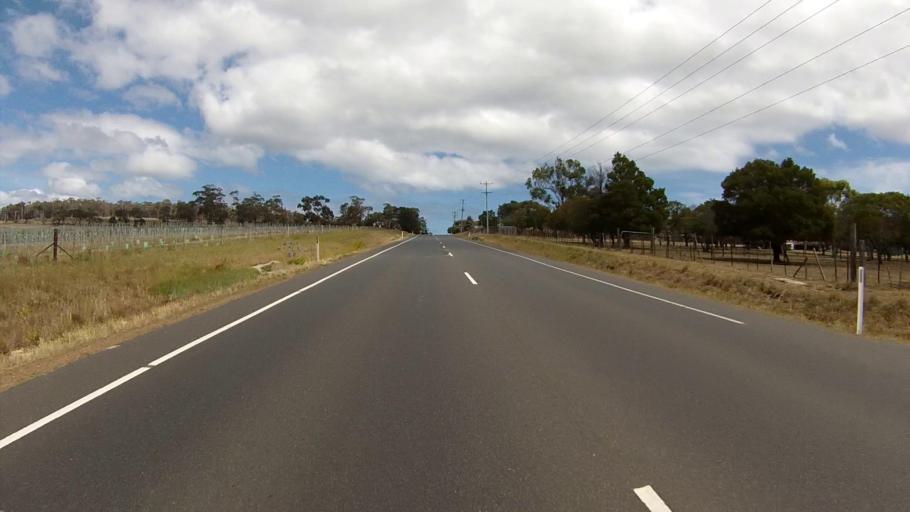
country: AU
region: Tasmania
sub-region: Sorell
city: Sorell
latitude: -42.8142
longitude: 147.6254
